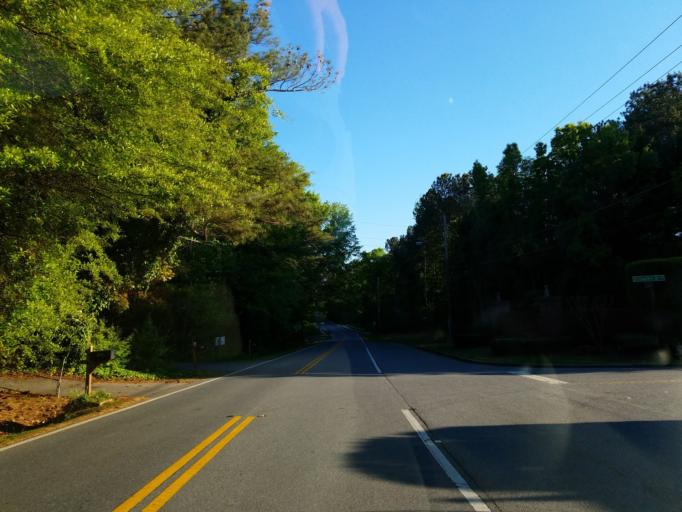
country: US
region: Georgia
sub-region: Cobb County
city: Kennesaw
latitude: 33.9378
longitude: -84.6407
